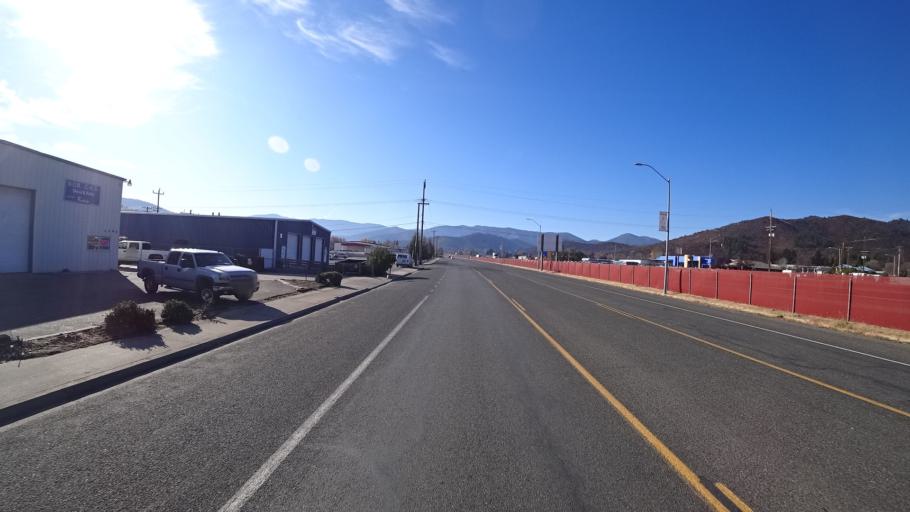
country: US
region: California
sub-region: Siskiyou County
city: Yreka
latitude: 41.7123
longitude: -122.6406
